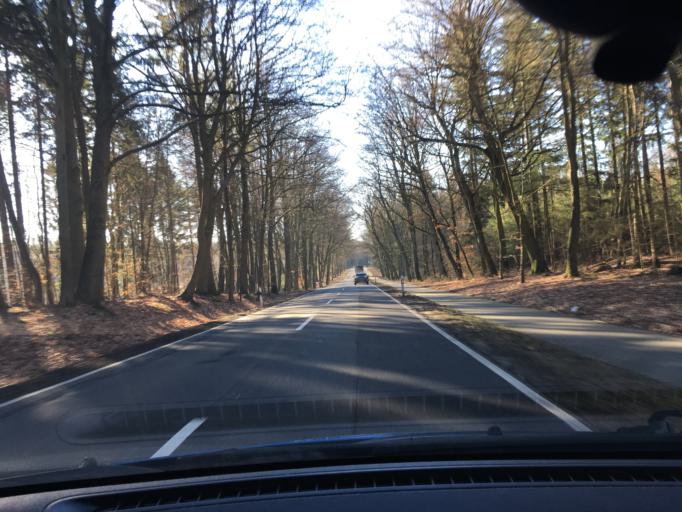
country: DE
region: Lower Saxony
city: Hanstedt Eins
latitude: 53.0773
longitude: 10.4051
